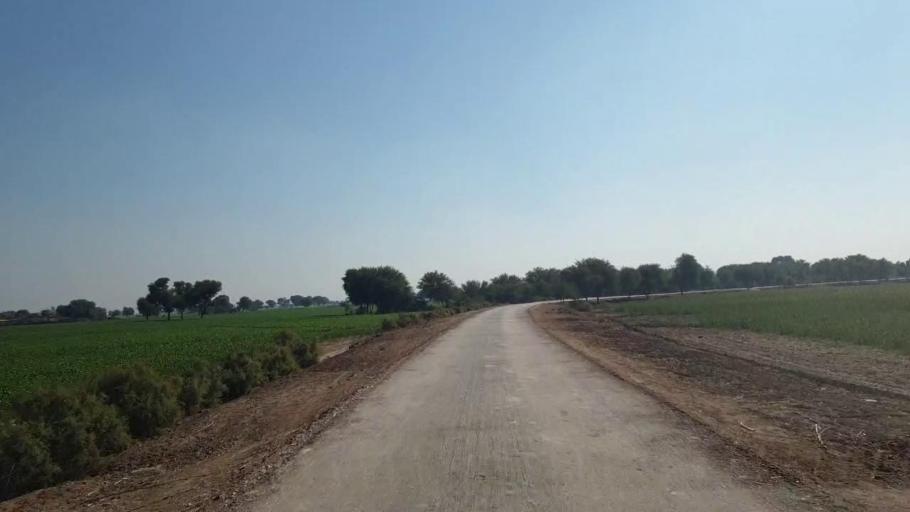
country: PK
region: Sindh
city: Shahpur Chakar
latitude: 26.1195
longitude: 68.6278
